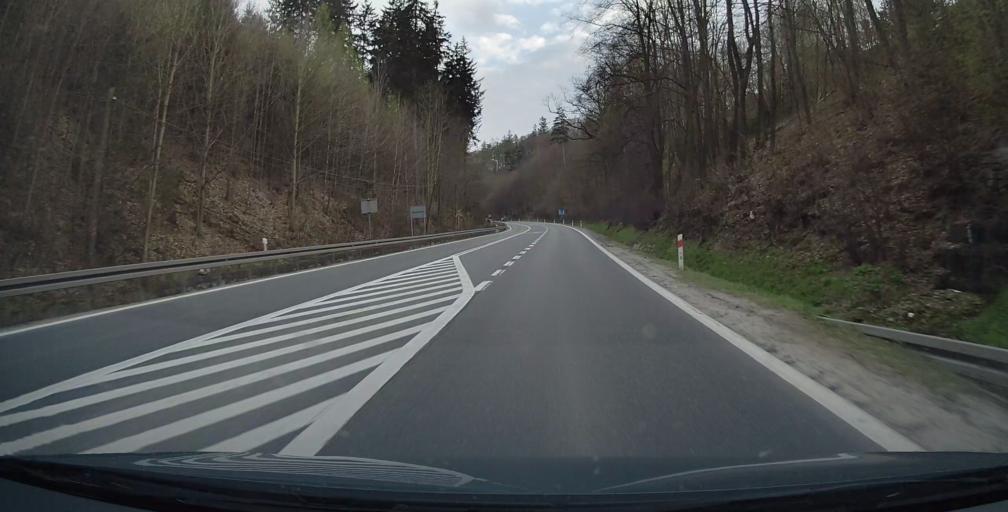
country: PL
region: Lower Silesian Voivodeship
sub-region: Powiat zabkowicki
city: Bardo
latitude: 50.4873
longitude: 16.7156
